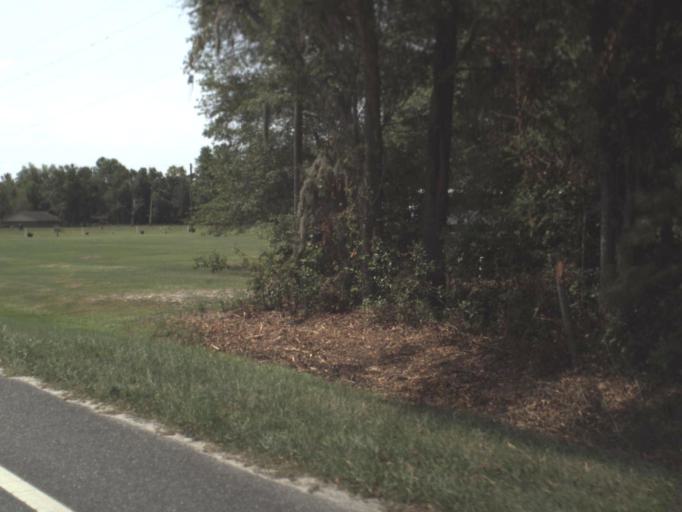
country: US
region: Georgia
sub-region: Echols County
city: Statenville
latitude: 30.6079
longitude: -83.1049
